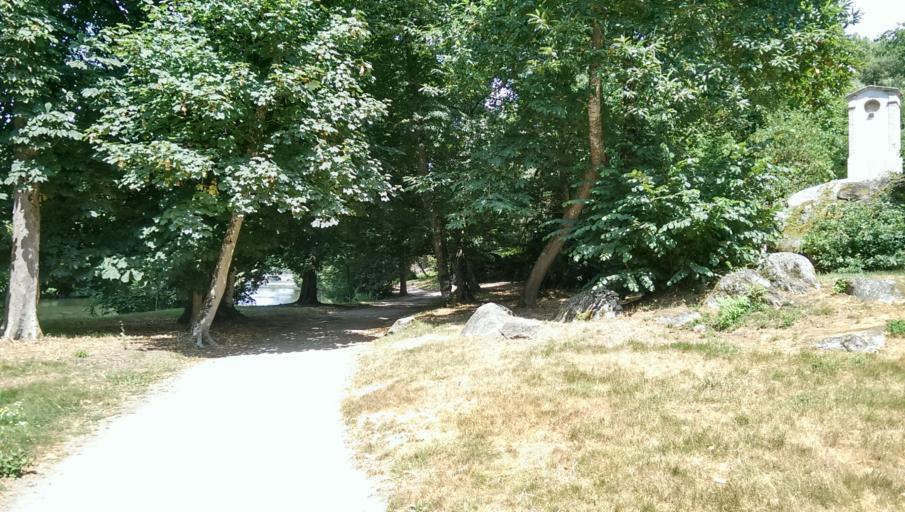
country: FR
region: Pays de la Loire
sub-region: Departement de la Loire-Atlantique
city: Clisson
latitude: 47.0835
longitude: -1.2752
